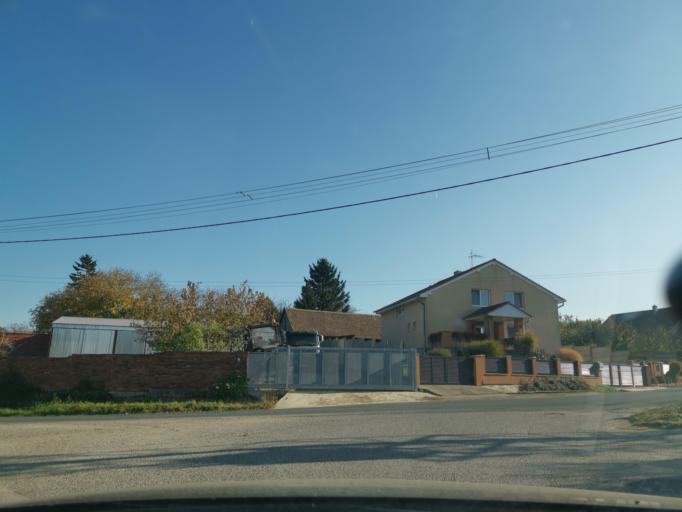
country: SK
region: Trnavsky
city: Gbely
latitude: 48.7243
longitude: 17.2079
